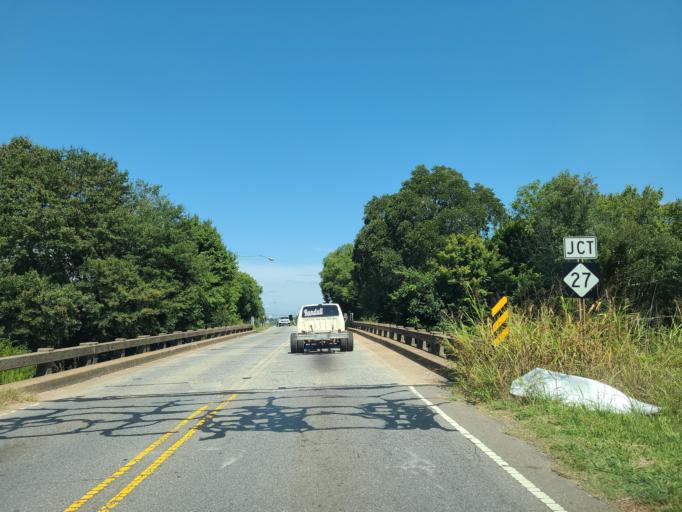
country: US
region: North Carolina
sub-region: Lincoln County
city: Lincolnton
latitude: 35.4745
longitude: -81.2396
